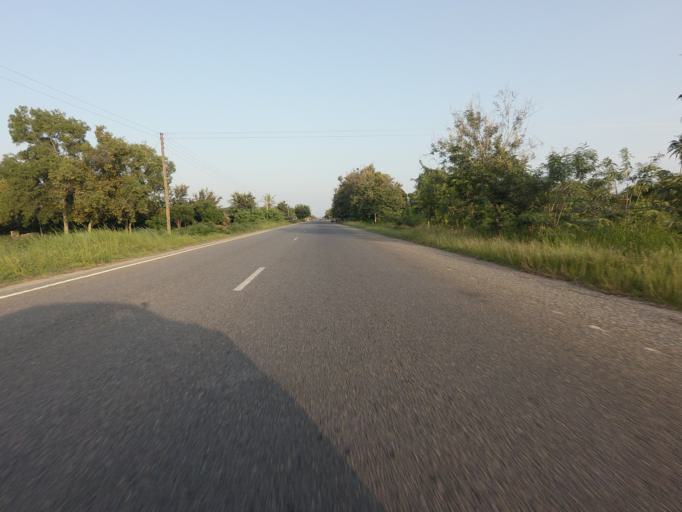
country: GH
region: Volta
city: Anloga
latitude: 5.8936
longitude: 0.7167
